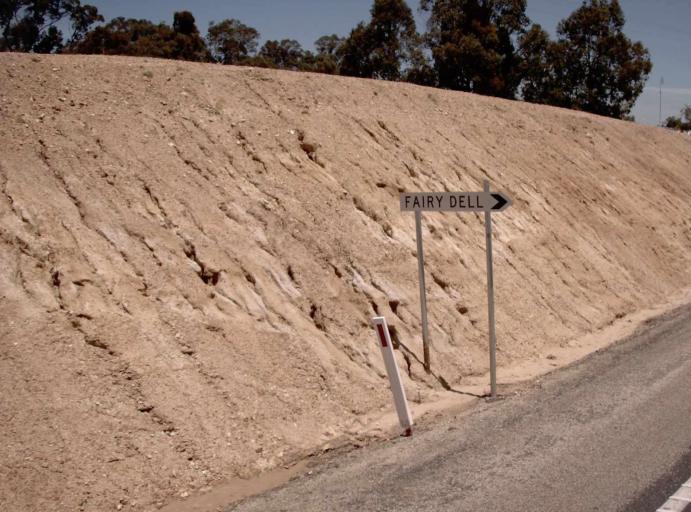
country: AU
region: Victoria
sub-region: East Gippsland
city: Bairnsdale
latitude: -37.7123
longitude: 147.8079
